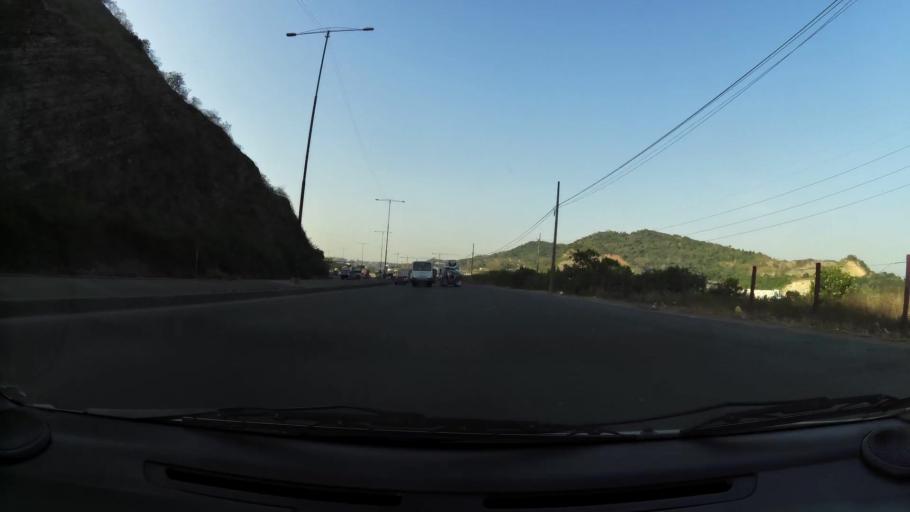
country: EC
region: Guayas
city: Guayaquil
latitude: -2.1847
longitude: -79.9498
